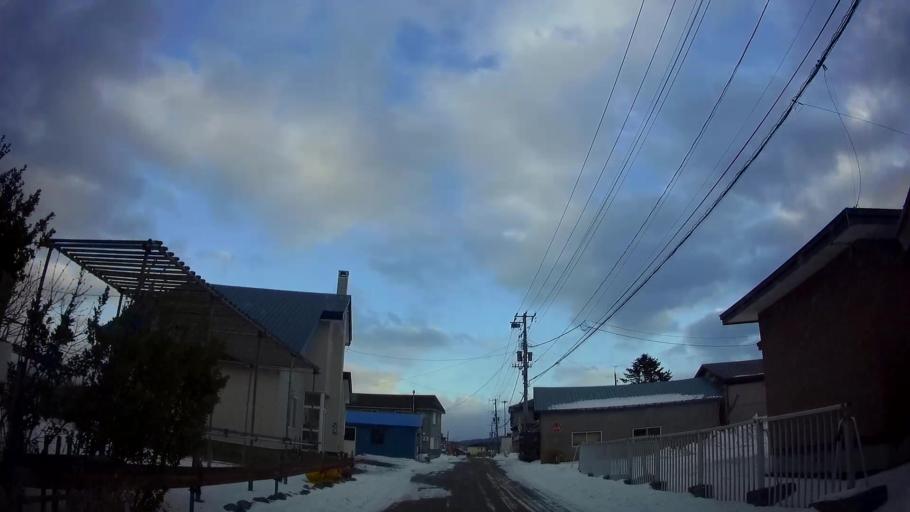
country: JP
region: Hokkaido
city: Nanae
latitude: 42.0400
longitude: 140.8165
